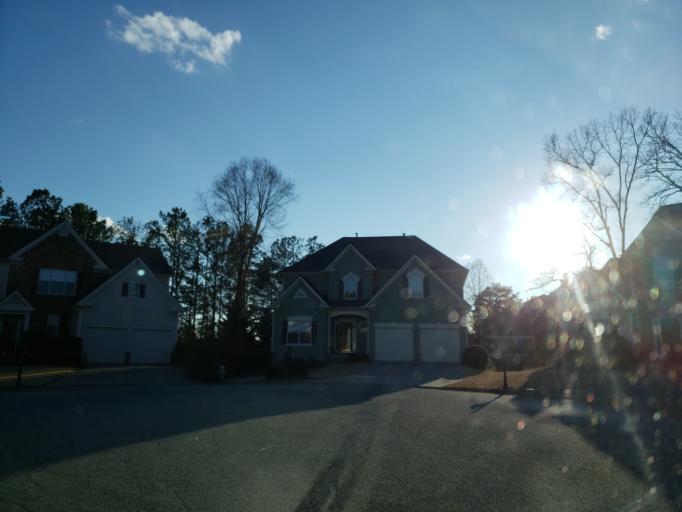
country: US
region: Georgia
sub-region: Cherokee County
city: Woodstock
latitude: 34.0443
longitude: -84.4806
